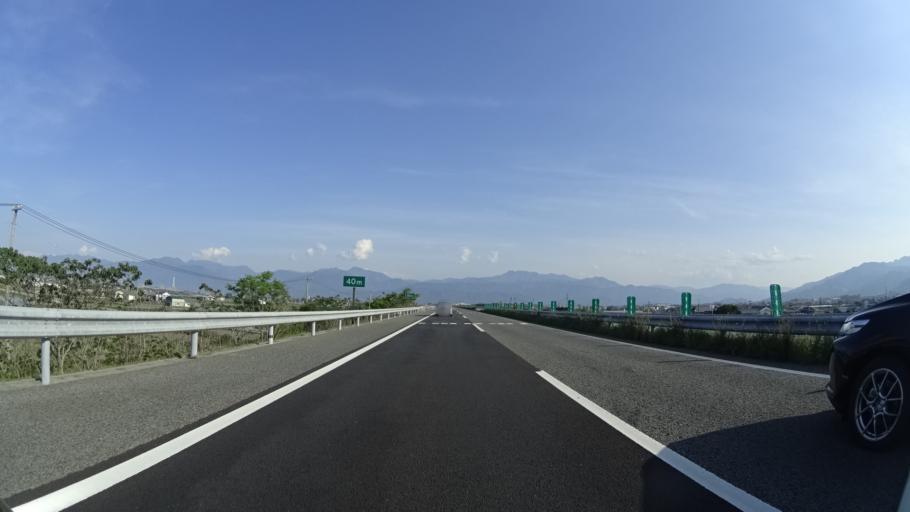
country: JP
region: Ehime
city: Saijo
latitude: 33.9613
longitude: 133.0647
